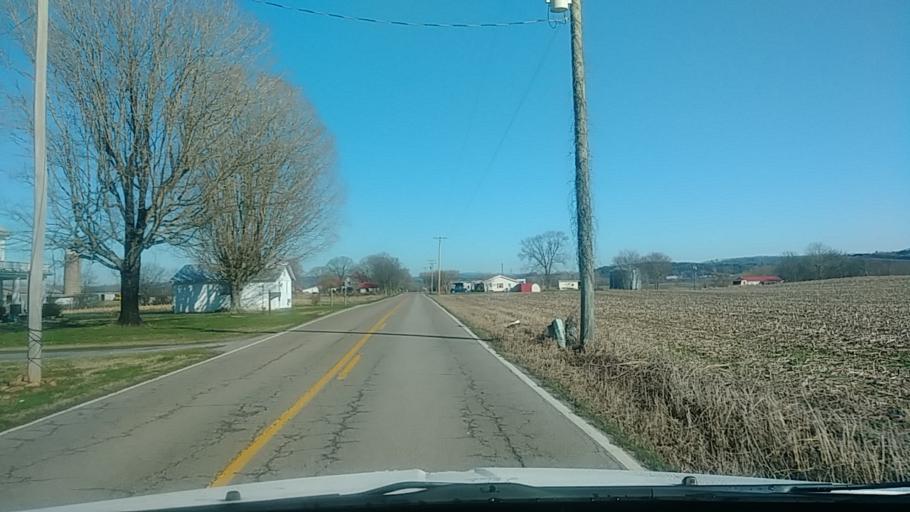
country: US
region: Tennessee
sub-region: Jefferson County
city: White Pine
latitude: 36.1594
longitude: -83.1622
